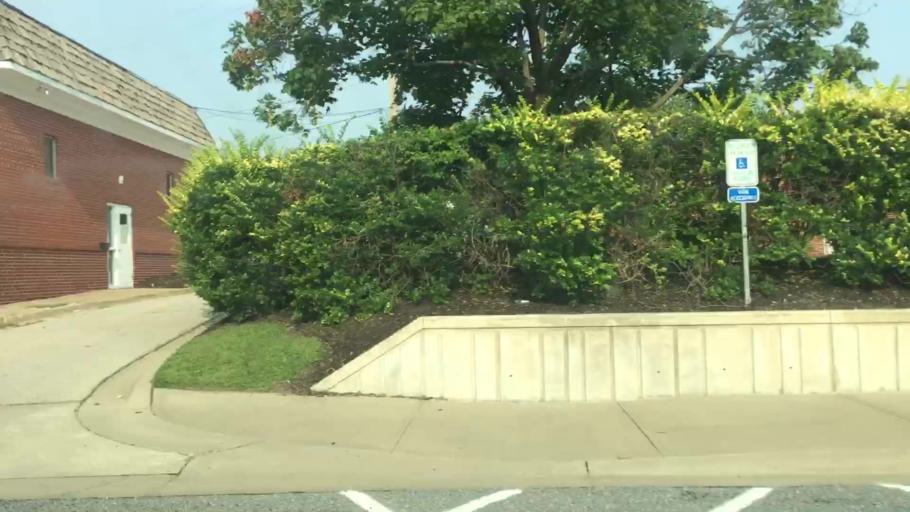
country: US
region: Kansas
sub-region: Johnson County
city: Overland Park
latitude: 38.9832
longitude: -94.6735
